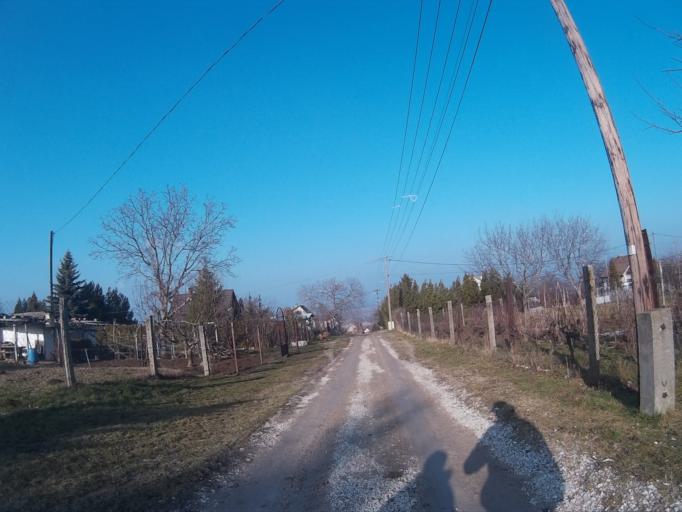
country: HU
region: Komarom-Esztergom
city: Labatlan
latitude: 47.7428
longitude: 18.4831
